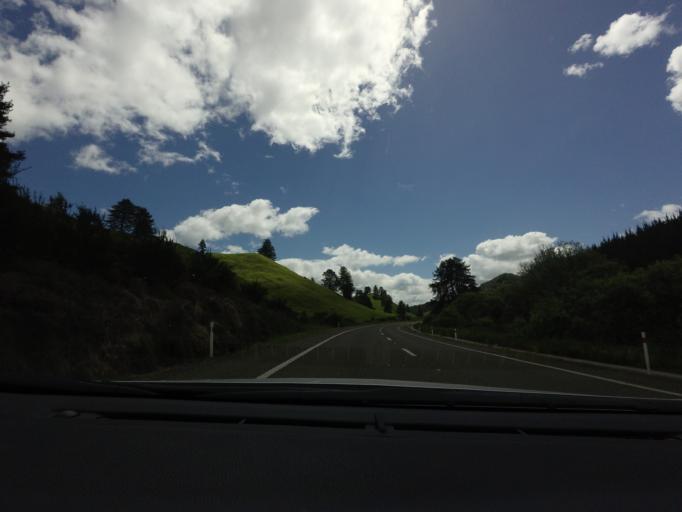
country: NZ
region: Bay of Plenty
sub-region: Rotorua District
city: Rotorua
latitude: -38.2220
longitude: 176.2846
